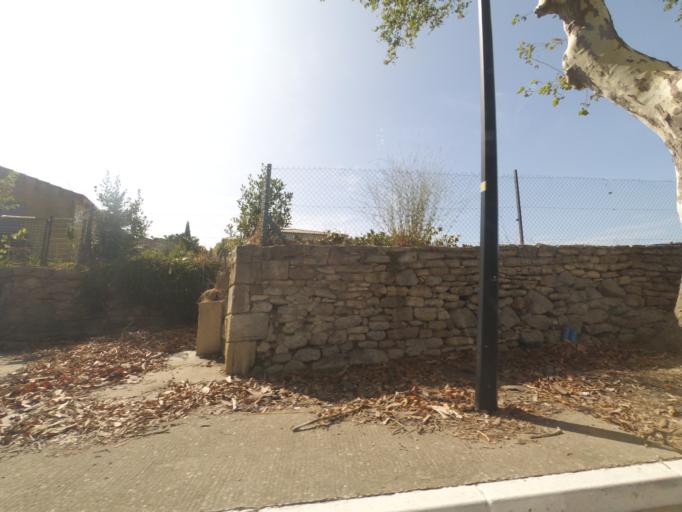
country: FR
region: Languedoc-Roussillon
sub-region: Departement du Gard
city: Villevieille
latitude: 43.8157
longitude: 4.1235
